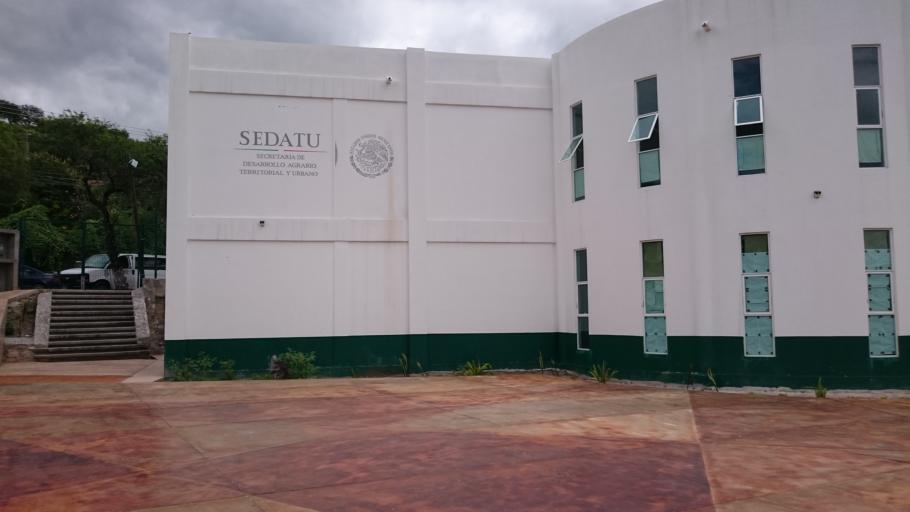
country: MX
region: Oaxaca
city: Ciudad de Huajuapam de Leon
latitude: 17.8173
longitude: -97.7750
